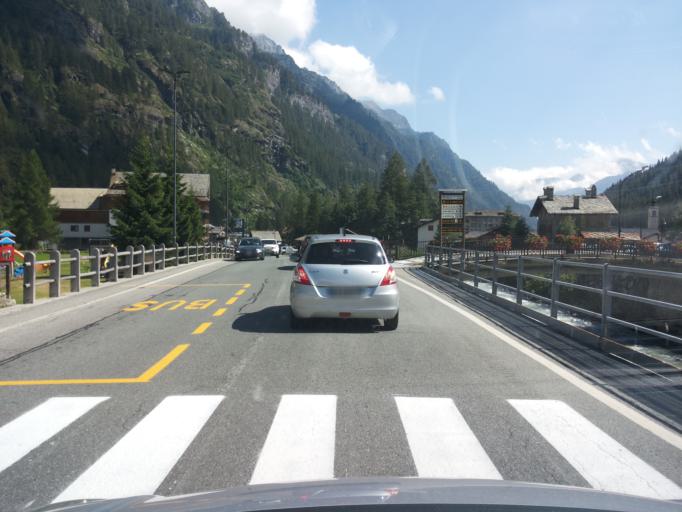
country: IT
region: Aosta Valley
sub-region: Valle d'Aosta
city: Gressoney-La-Trinite
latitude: 45.8307
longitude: 7.8231
